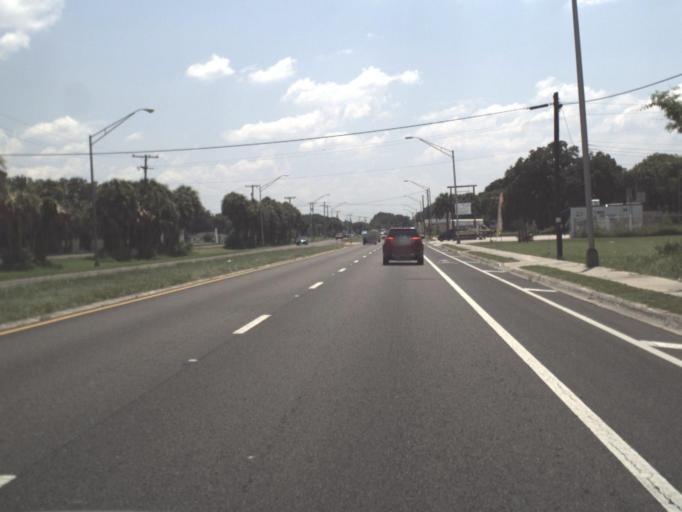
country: US
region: Florida
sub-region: Hillsborough County
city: Gibsonton
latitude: 27.8546
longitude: -82.3827
